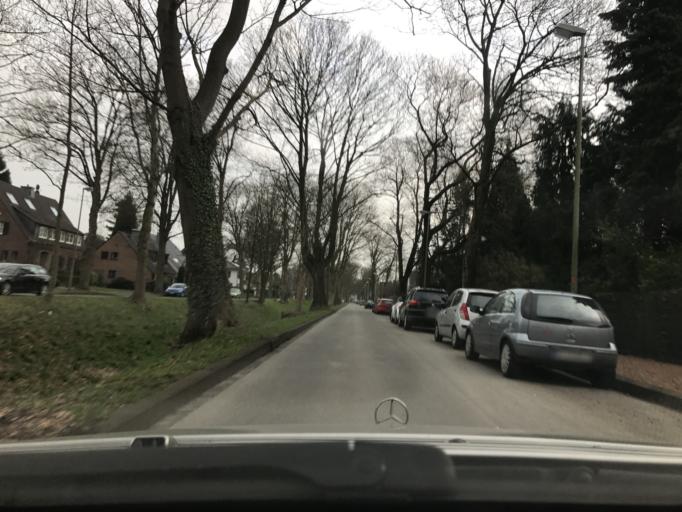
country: DE
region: North Rhine-Westphalia
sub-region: Regierungsbezirk Dusseldorf
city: Krefeld
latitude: 51.3459
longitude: 6.5788
